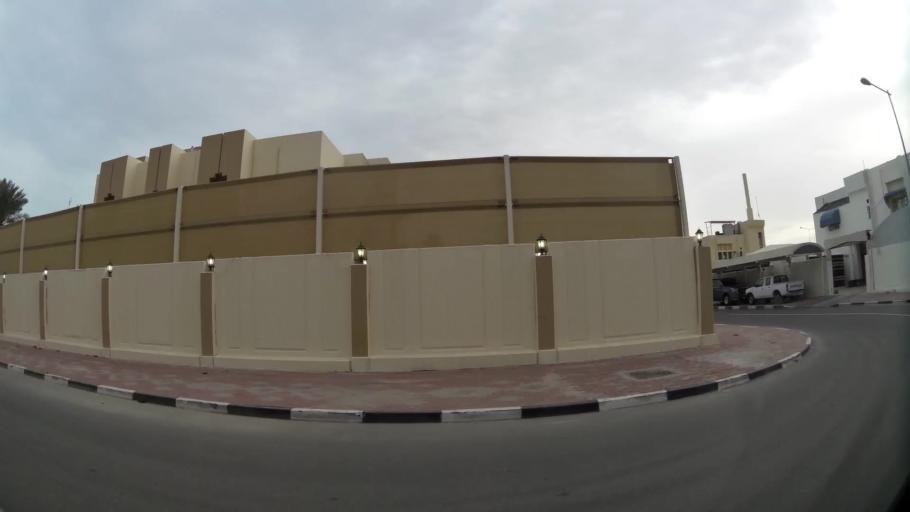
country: QA
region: Baladiyat ad Dawhah
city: Doha
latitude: 25.3348
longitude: 51.5068
